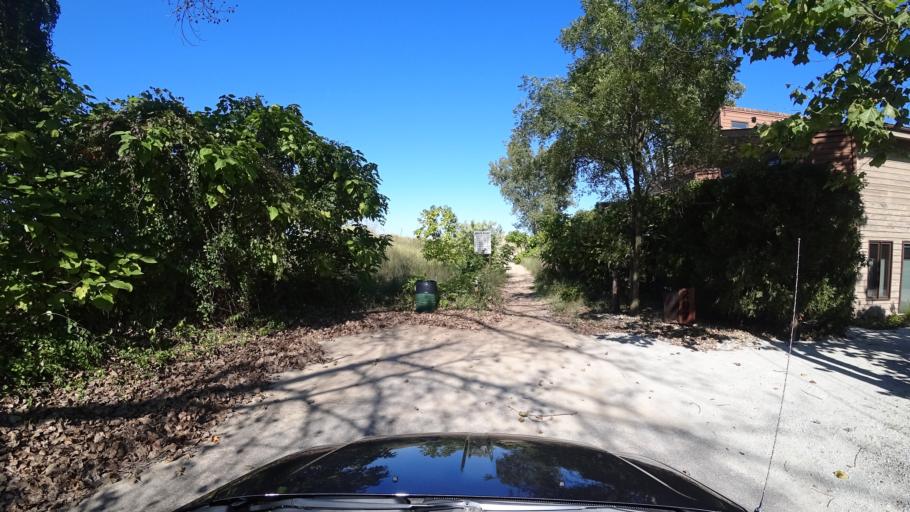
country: US
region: Indiana
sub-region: LaPorte County
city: Michigan City
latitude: 41.7313
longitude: -86.8895
